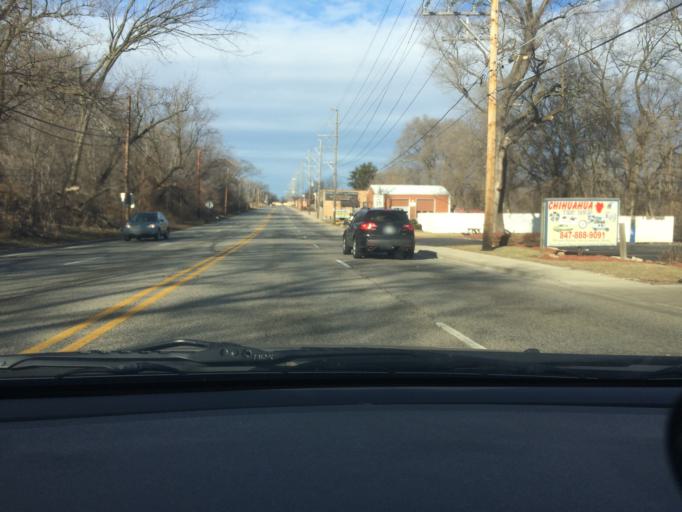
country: US
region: Illinois
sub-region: Kane County
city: Elgin
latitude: 42.0458
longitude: -88.2938
